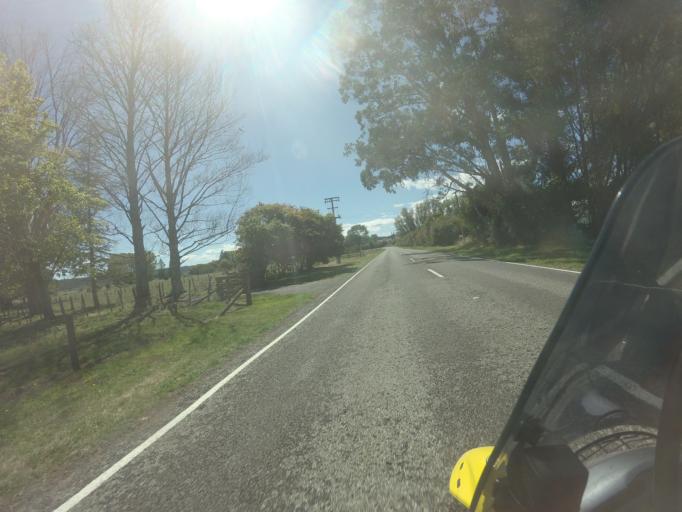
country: NZ
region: Bay of Plenty
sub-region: Whakatane District
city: Murupara
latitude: -38.3374
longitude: 176.7949
